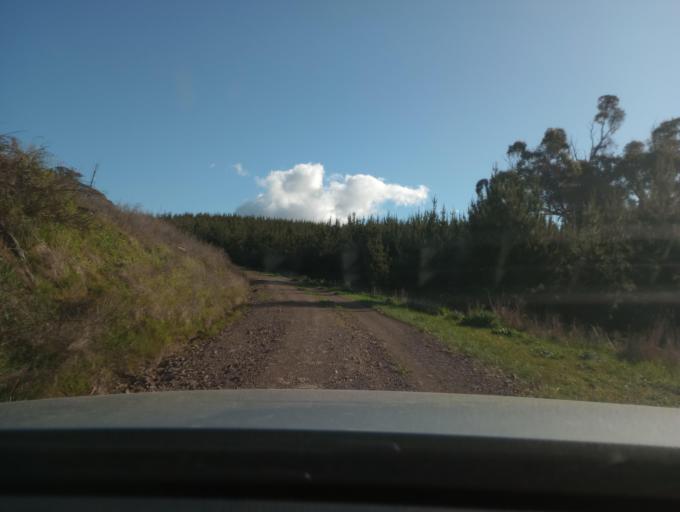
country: AU
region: New South Wales
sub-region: Blayney
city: Blayney
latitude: -33.4138
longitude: 149.3153
